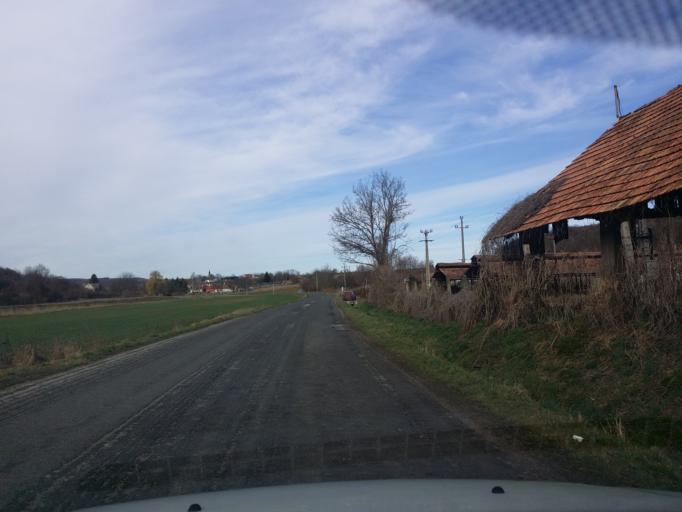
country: HU
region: Baranya
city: Villany
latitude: 45.8786
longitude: 18.4391
